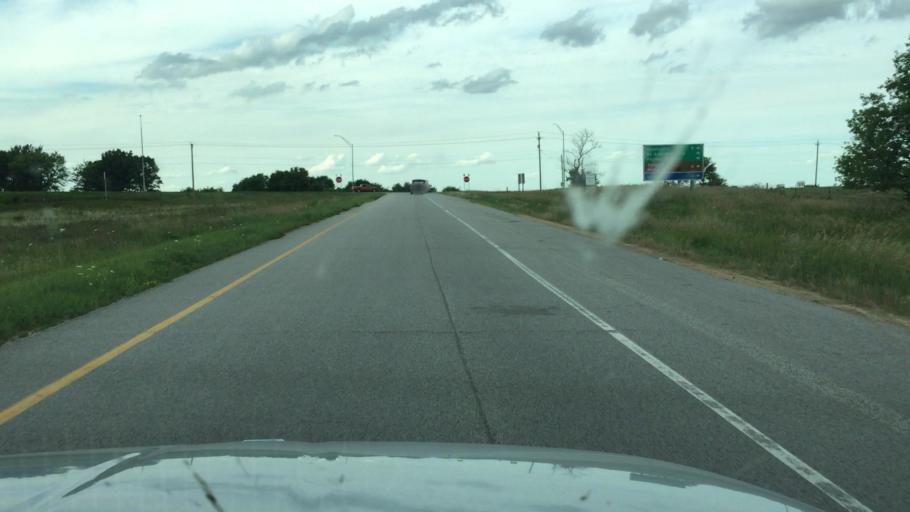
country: US
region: Iowa
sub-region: Scott County
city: Buffalo
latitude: 41.5365
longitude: -90.6751
